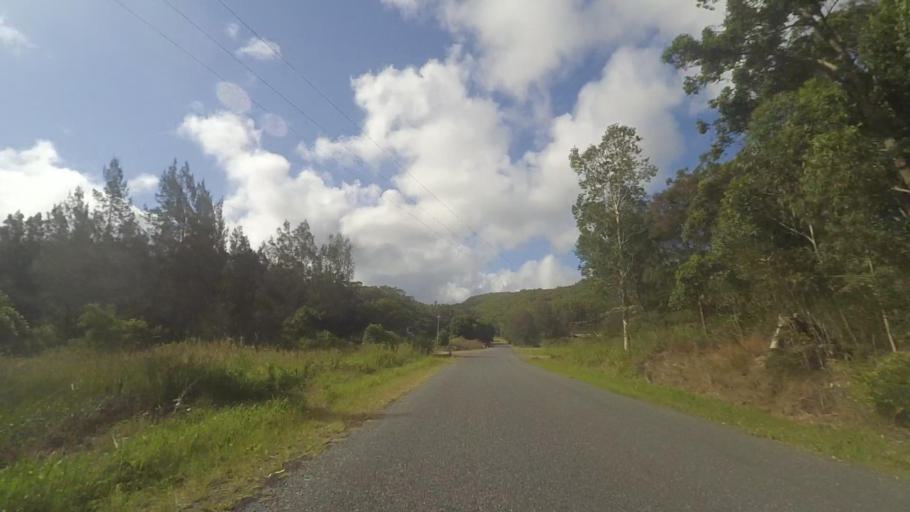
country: AU
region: New South Wales
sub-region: Great Lakes
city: Forster
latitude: -32.4012
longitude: 152.4603
